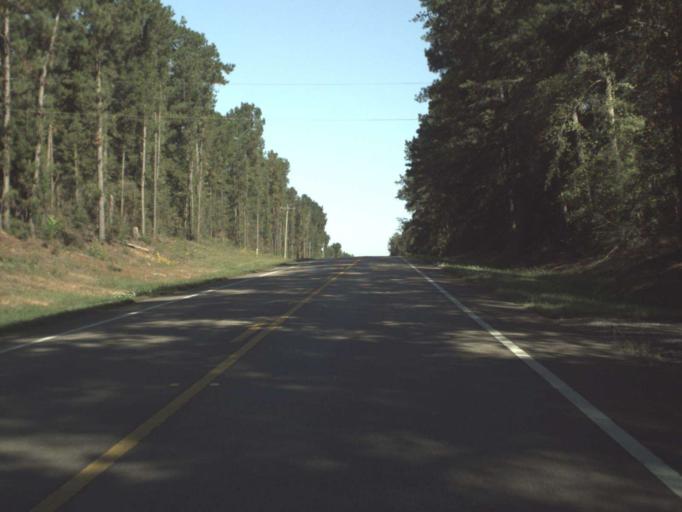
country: US
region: Florida
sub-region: Walton County
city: DeFuniak Springs
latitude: 30.6811
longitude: -85.9365
